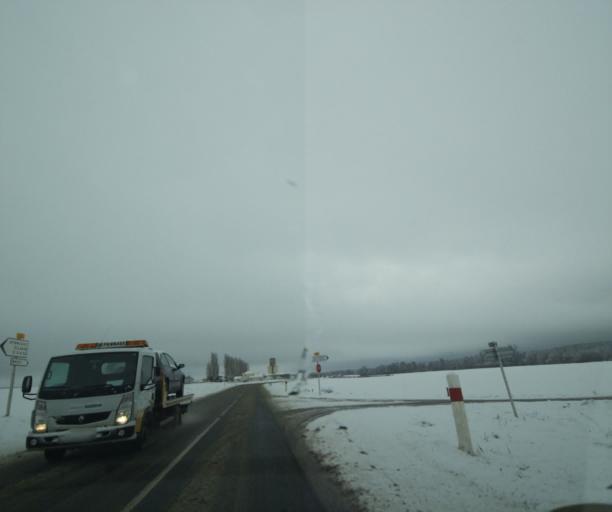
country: FR
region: Champagne-Ardenne
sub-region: Departement de la Haute-Marne
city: Wassy
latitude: 48.5173
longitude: 4.9353
